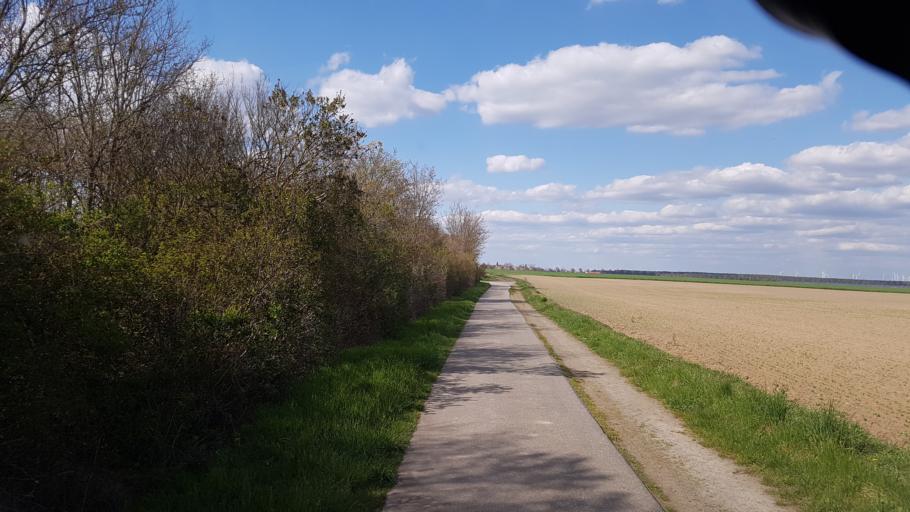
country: DE
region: Brandenburg
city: Muhlberg
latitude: 51.4562
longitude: 13.2685
